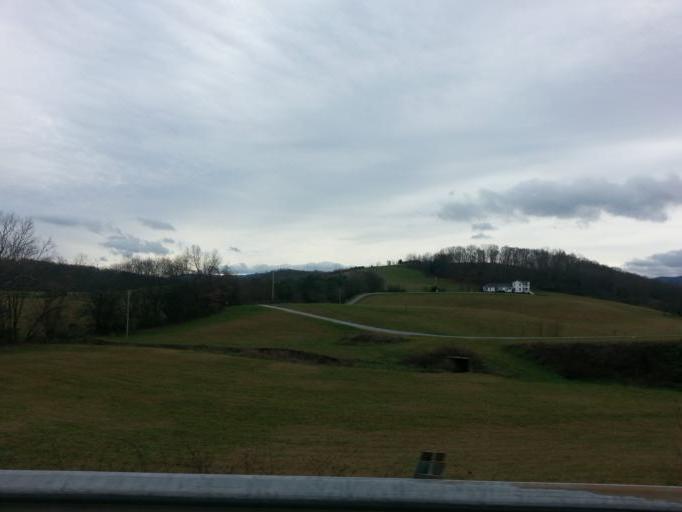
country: US
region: Tennessee
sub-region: Greene County
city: Mosheim
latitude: 36.0794
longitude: -82.9600
